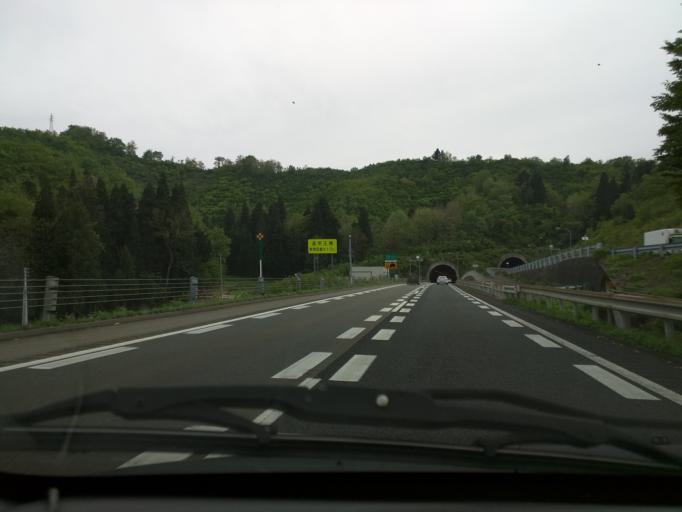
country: JP
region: Niigata
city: Muikamachi
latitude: 37.1988
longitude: 138.9619
